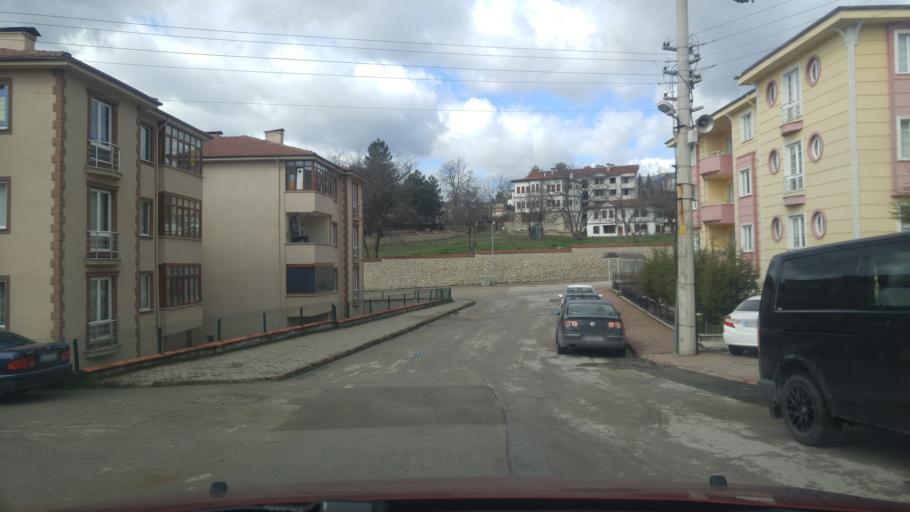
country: TR
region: Karabuk
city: Safranbolu
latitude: 41.2597
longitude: 32.6817
